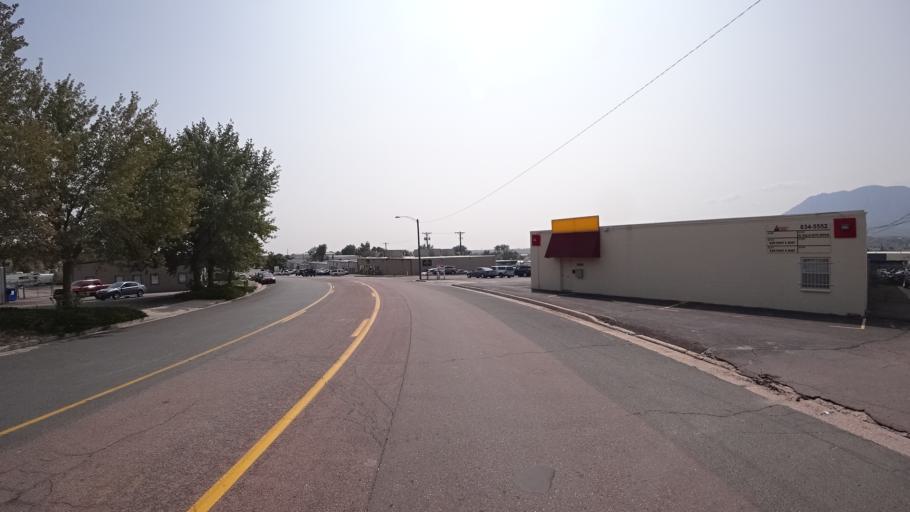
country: US
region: Colorado
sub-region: El Paso County
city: Stratmoor
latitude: 38.7963
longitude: -104.7776
